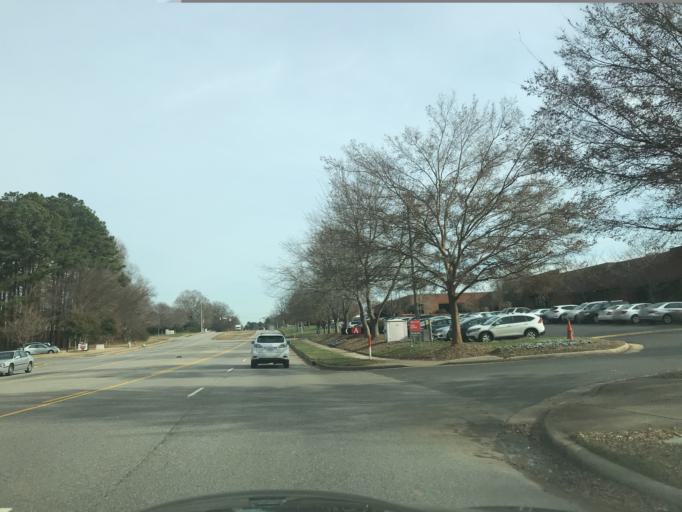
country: US
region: North Carolina
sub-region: Wake County
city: Raleigh
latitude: 35.8552
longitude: -78.5891
